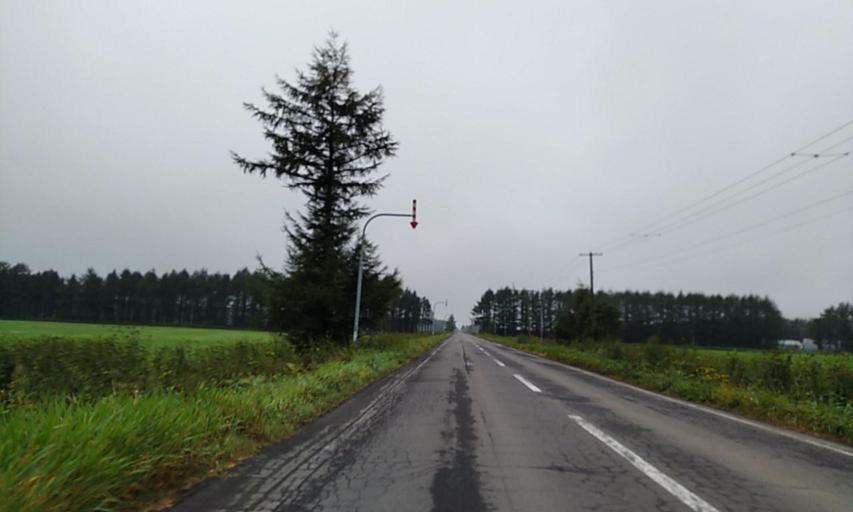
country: JP
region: Hokkaido
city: Shibetsu
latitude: 43.5146
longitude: 144.6763
